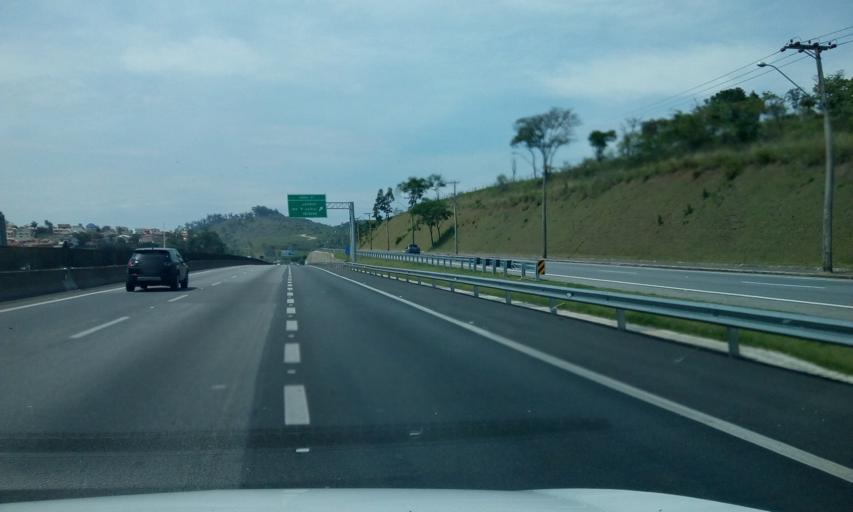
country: BR
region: Sao Paulo
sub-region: Jundiai
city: Jundiai
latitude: -23.1955
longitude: -46.9044
